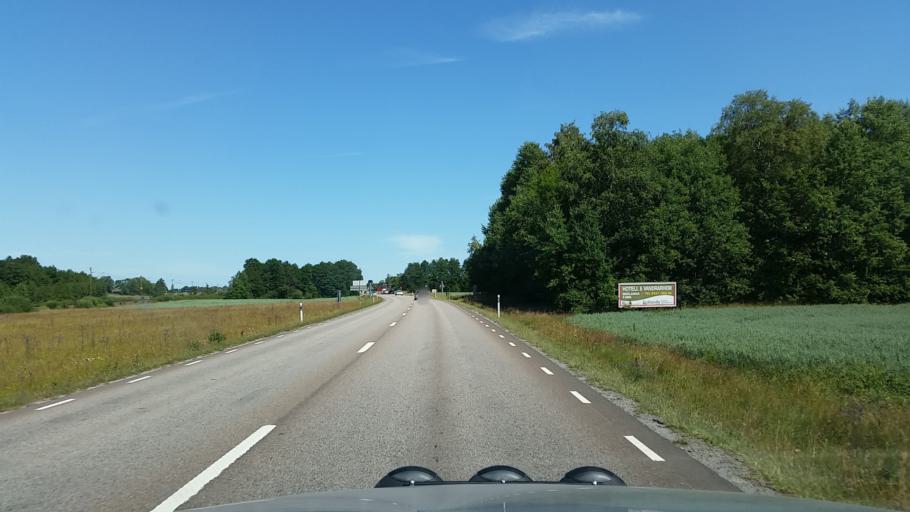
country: SE
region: Vaestra Goetaland
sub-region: Vanersborgs Kommun
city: Bralanda
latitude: 58.5087
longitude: 12.2896
